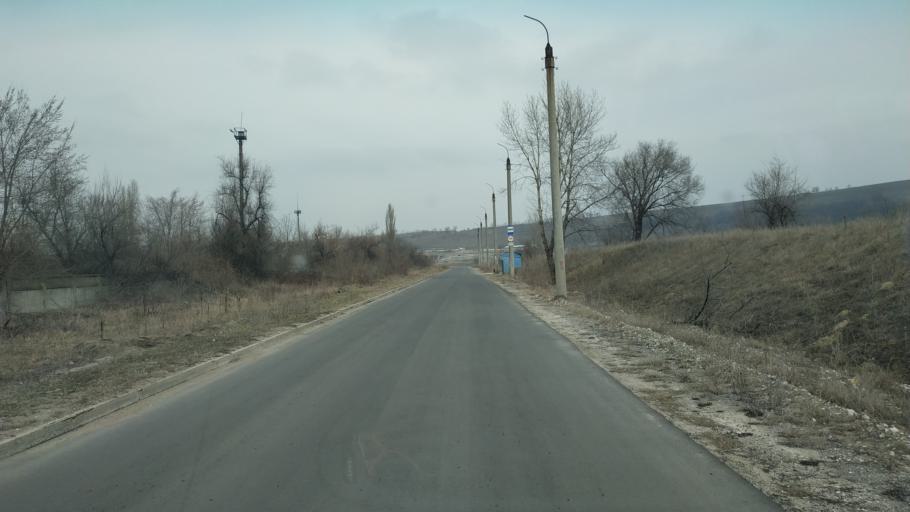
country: MD
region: Chisinau
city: Singera
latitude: 46.8957
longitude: 29.0193
